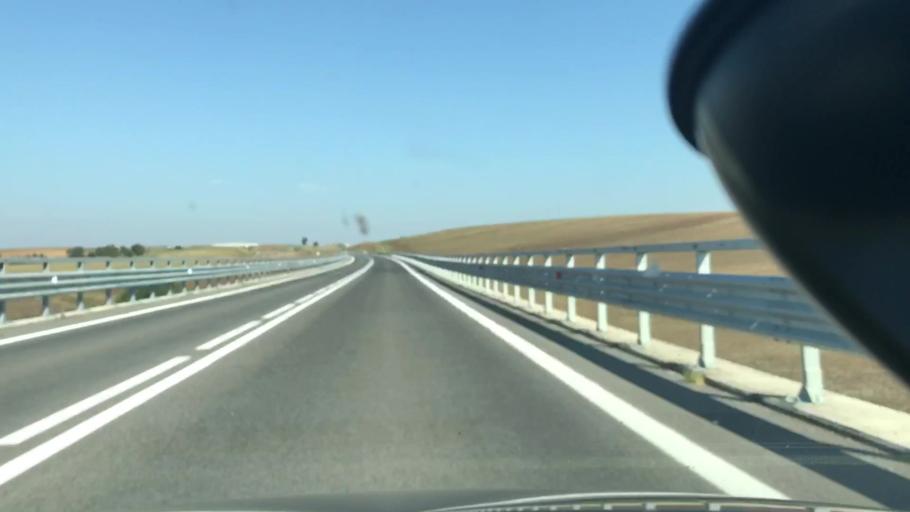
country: IT
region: Basilicate
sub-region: Provincia di Potenza
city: Palazzo San Gervasio
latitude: 40.9625
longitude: 16.0118
